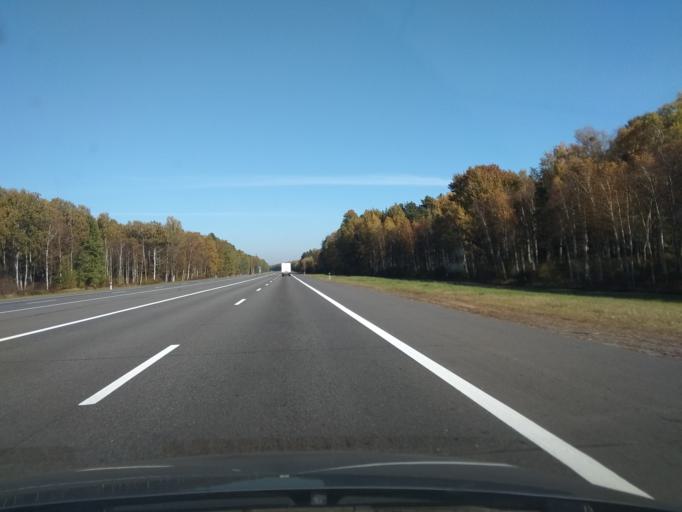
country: BY
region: Brest
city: Ivatsevichy
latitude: 52.7624
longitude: 25.5230
